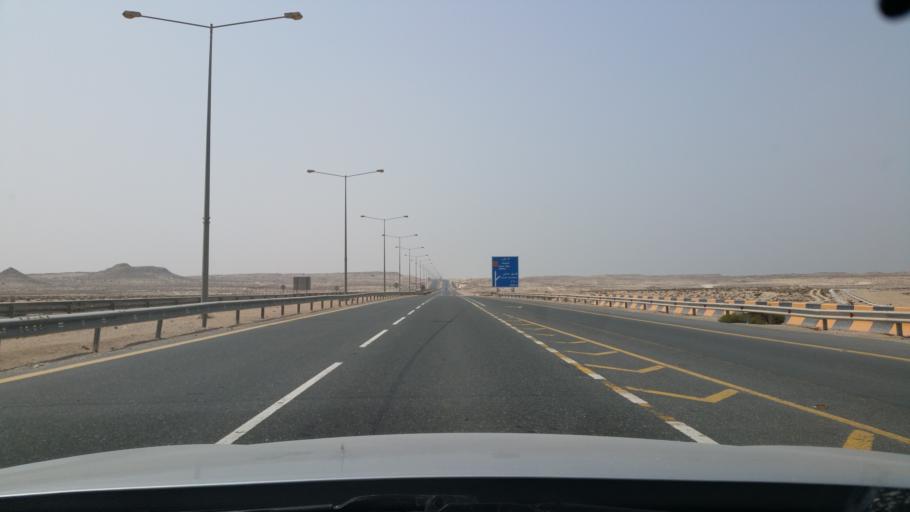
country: QA
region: Baladiyat ar Rayyan
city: Dukhan
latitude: 25.3715
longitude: 50.7805
